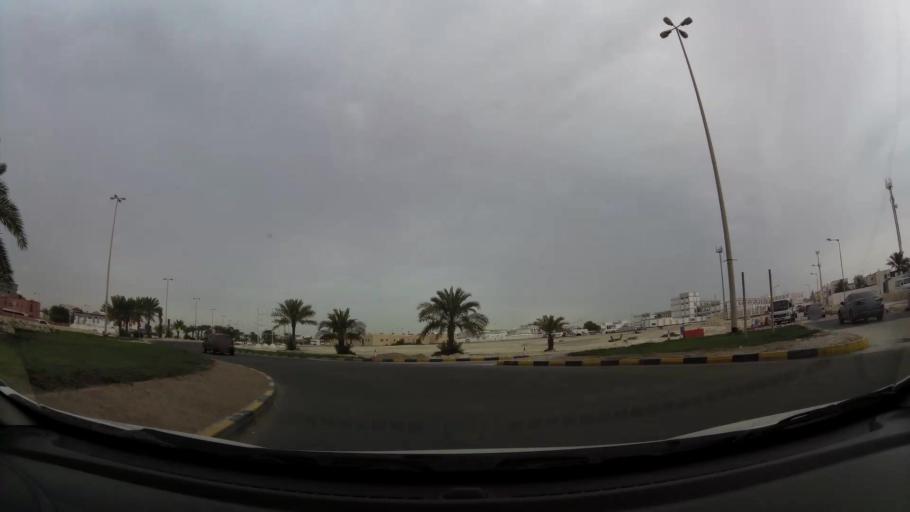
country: BH
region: Central Governorate
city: Dar Kulayb
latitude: 26.0684
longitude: 50.5079
